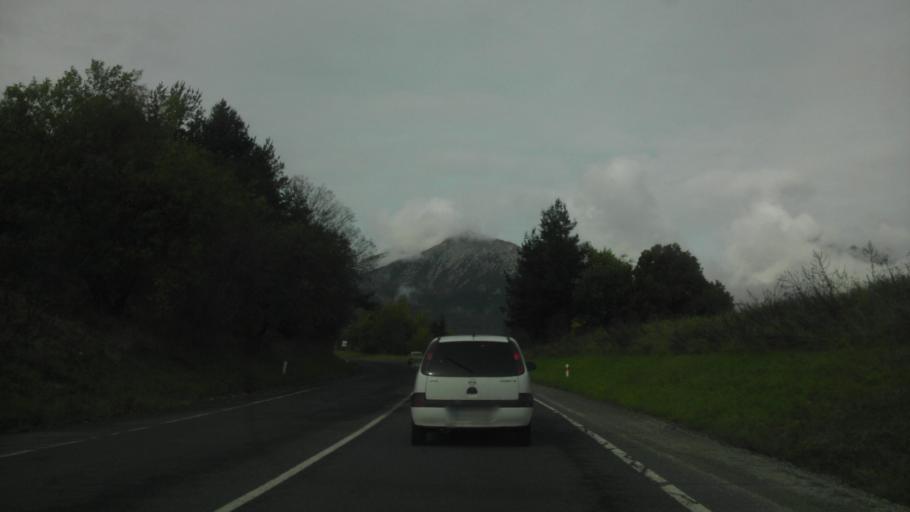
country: SK
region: Presovsky
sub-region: Okres Poprad
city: Nova Lesna
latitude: 49.1149
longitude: 20.2626
